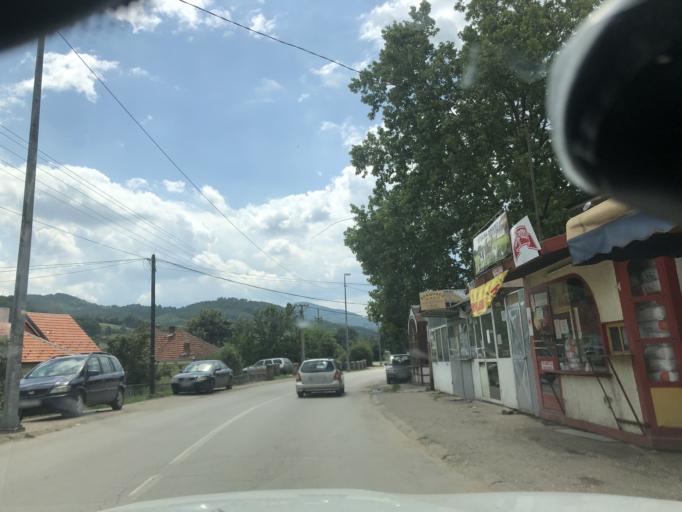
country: RS
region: Central Serbia
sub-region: Jablanicki Okrug
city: Medvega
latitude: 42.8435
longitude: 21.5872
